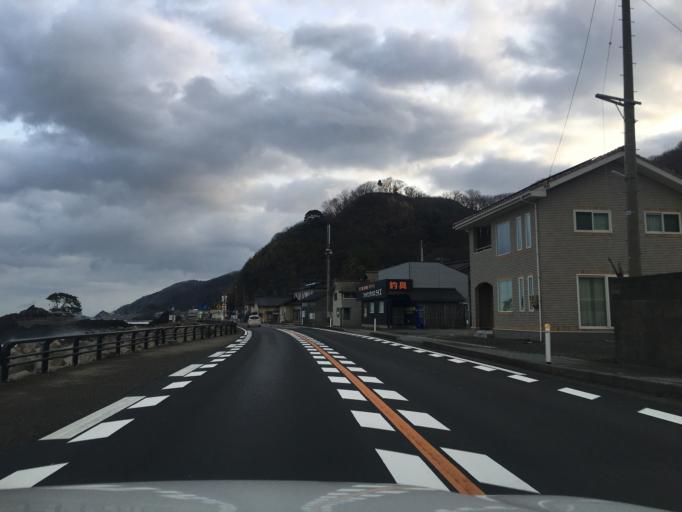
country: JP
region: Yamagata
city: Tsuruoka
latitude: 38.6179
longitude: 139.5819
